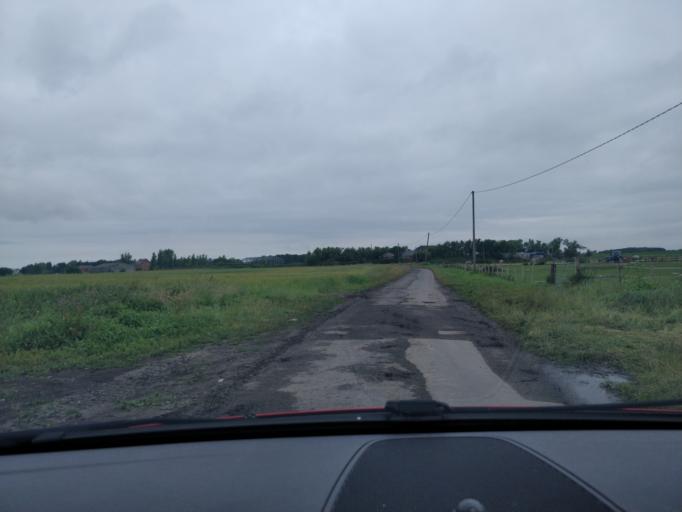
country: GB
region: England
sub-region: Lancashire
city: Banks
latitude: 53.6657
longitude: -2.9372
